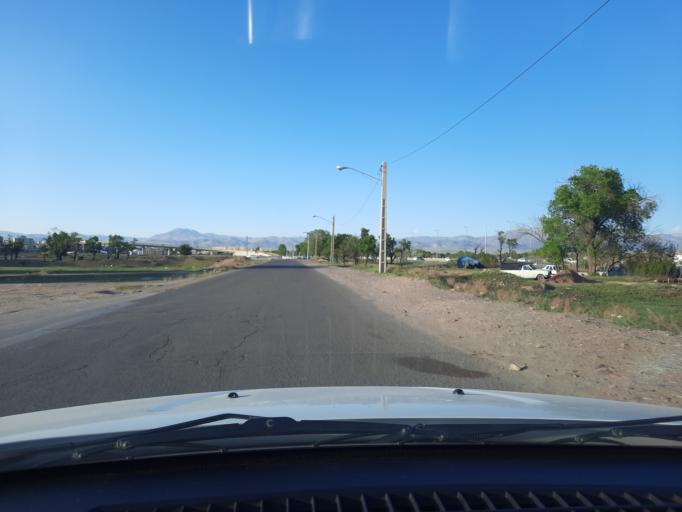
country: IR
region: Qazvin
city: Qazvin
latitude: 36.2678
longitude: 50.0248
